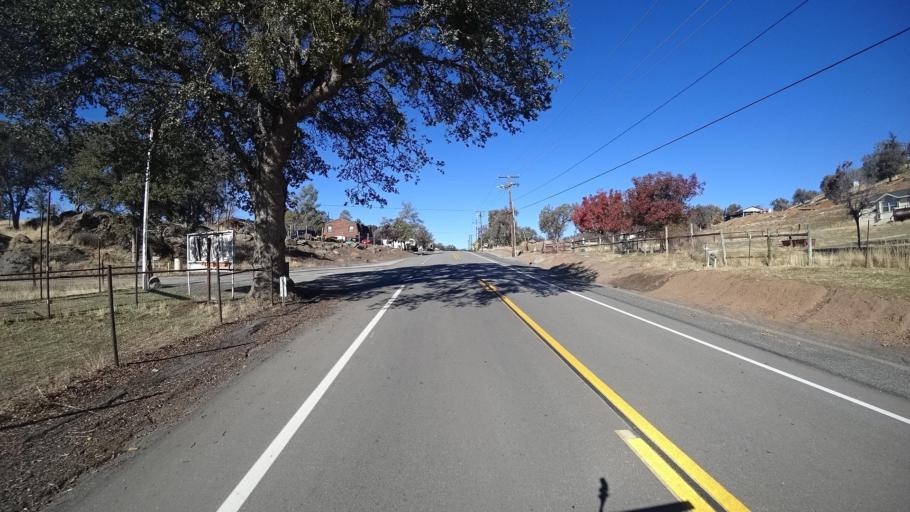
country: US
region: California
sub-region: Kern County
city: Alta Sierra
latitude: 35.7273
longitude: -118.7015
